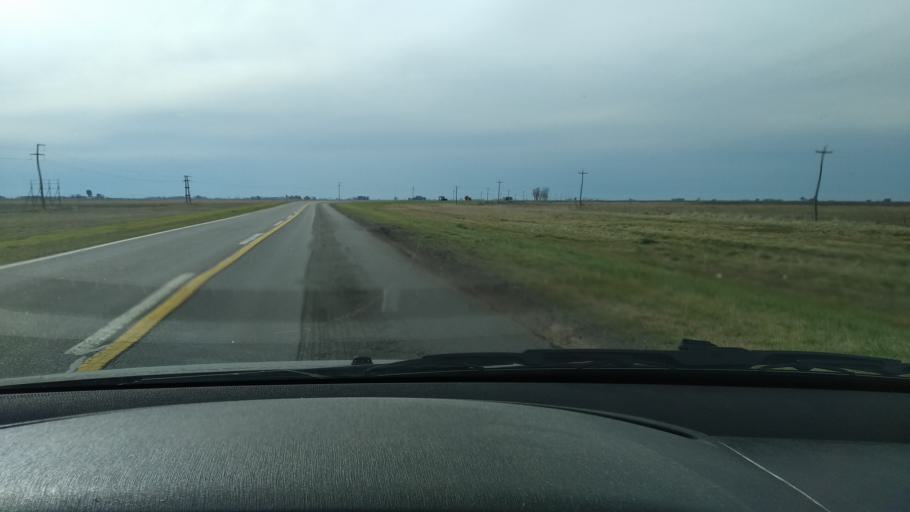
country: AR
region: Buenos Aires
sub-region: Partido de Azul
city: Azul
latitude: -36.7104
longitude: -59.7603
